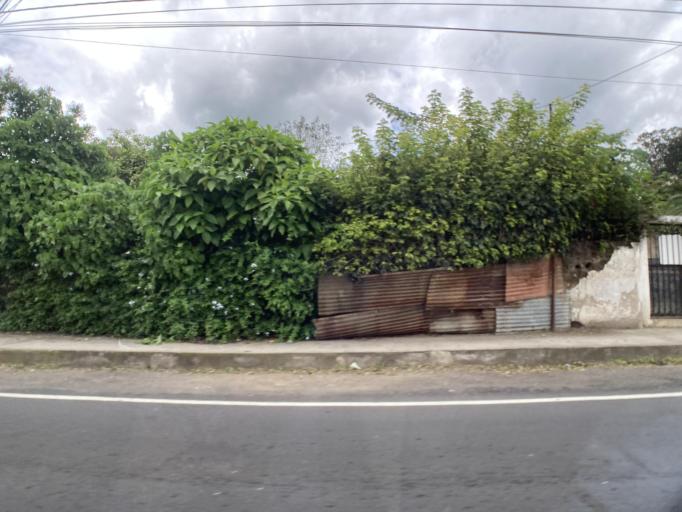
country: GT
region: Sacatepequez
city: Antigua Guatemala
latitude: 14.5688
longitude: -90.7356
